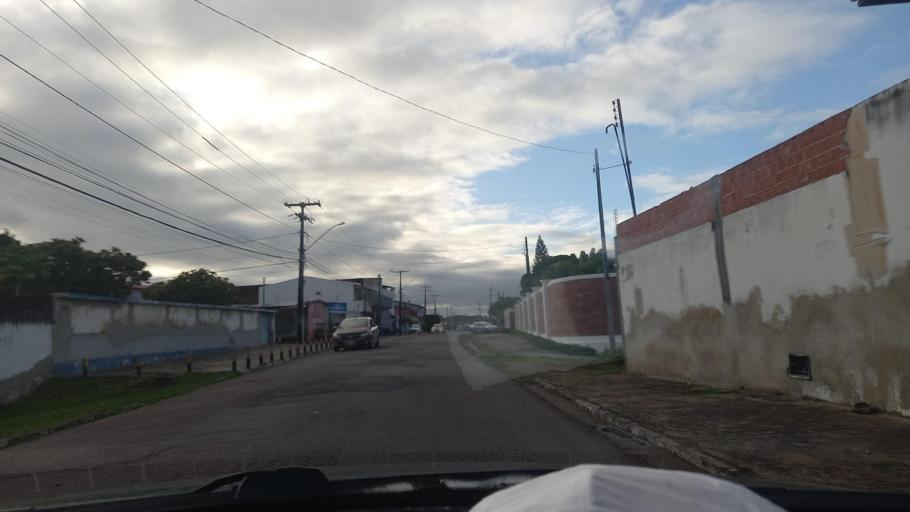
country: BR
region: Bahia
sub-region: Paulo Afonso
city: Paulo Afonso
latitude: -9.3951
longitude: -38.2378
